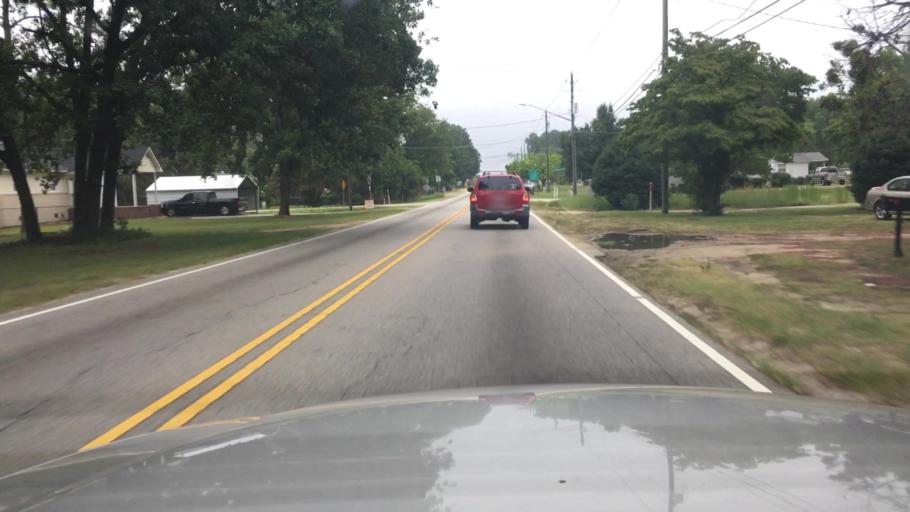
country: US
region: North Carolina
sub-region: Cumberland County
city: Hope Mills
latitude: 34.9830
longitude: -78.9711
